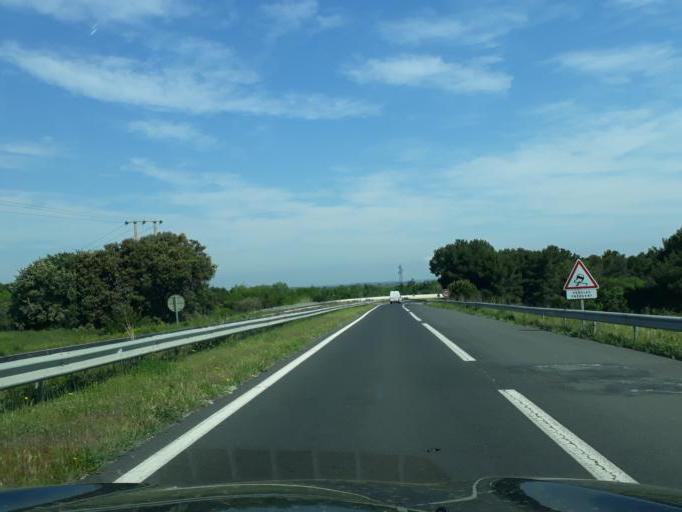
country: FR
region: Languedoc-Roussillon
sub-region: Departement de l'Herault
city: Le Cap d'Agde
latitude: 43.3065
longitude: 3.5080
